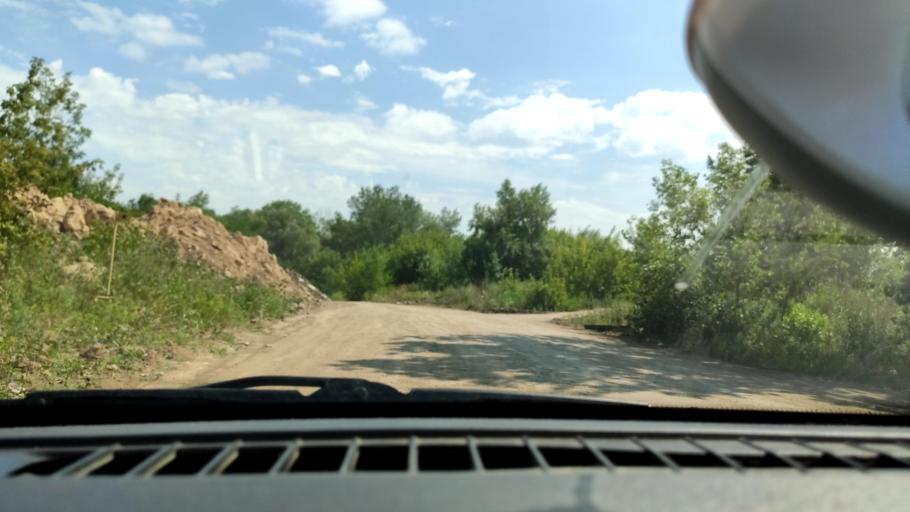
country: RU
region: Samara
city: Smyshlyayevka
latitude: 53.2052
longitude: 50.3193
